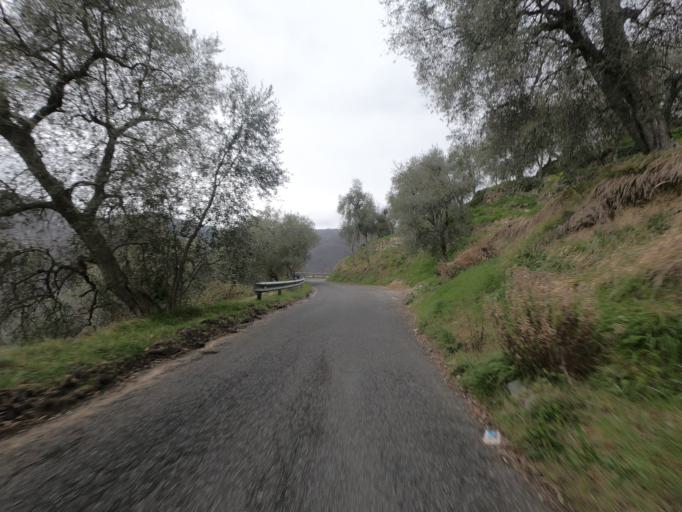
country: IT
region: Liguria
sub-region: Provincia di Savona
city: Testico
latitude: 44.0253
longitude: 8.0032
